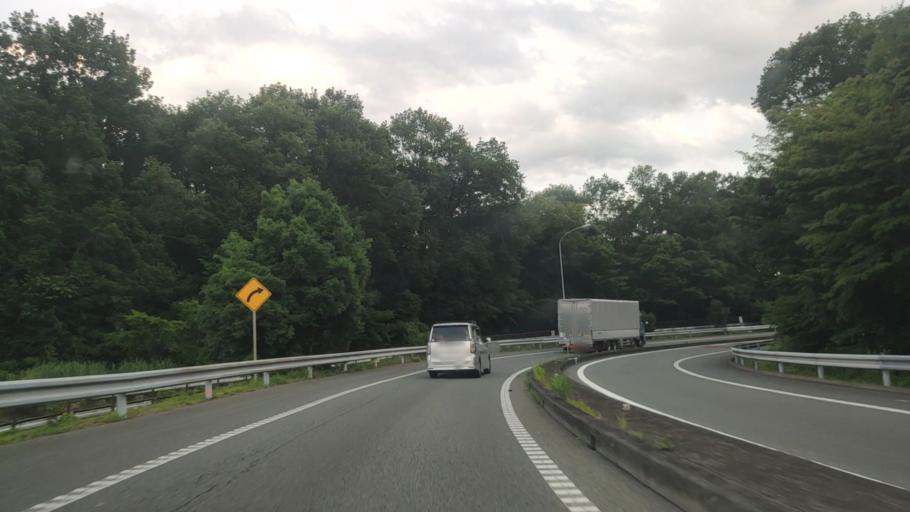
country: JP
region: Saitama
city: Hanno
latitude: 35.7967
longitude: 139.3235
